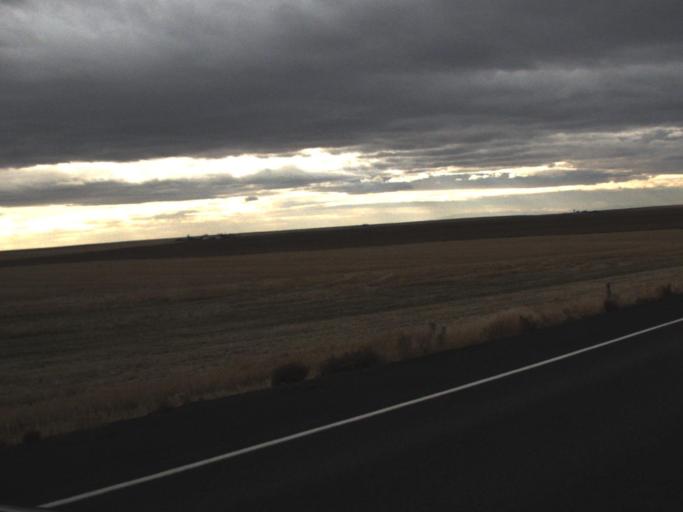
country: US
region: Washington
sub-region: Franklin County
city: Connell
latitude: 46.7945
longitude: -118.6226
